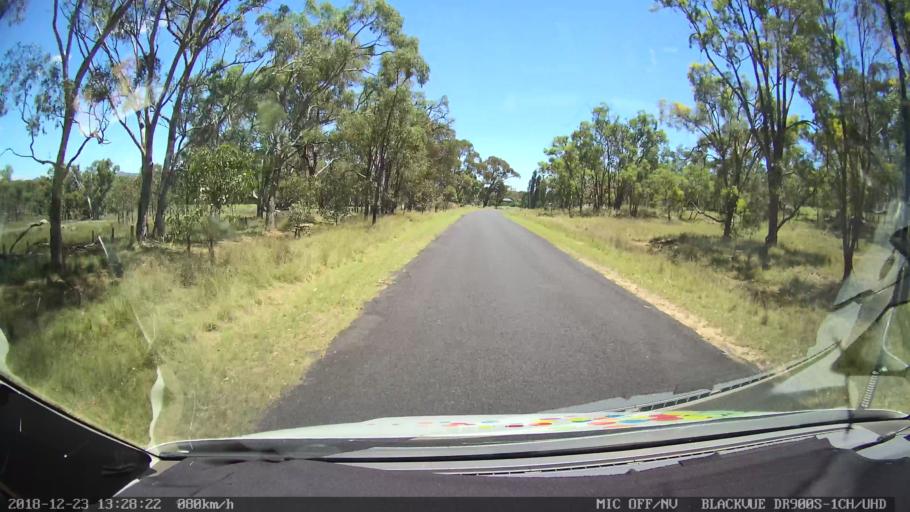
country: AU
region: New South Wales
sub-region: Armidale Dumaresq
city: Armidale
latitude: -30.4664
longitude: 151.3497
